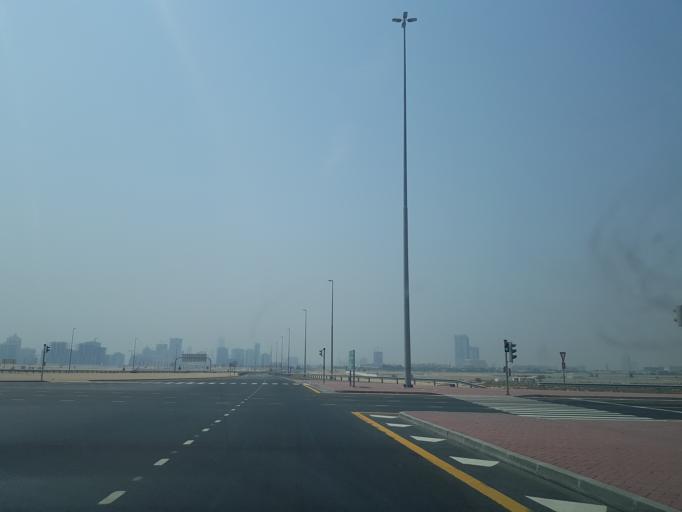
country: AE
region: Dubai
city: Dubai
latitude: 25.0246
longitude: 55.2400
